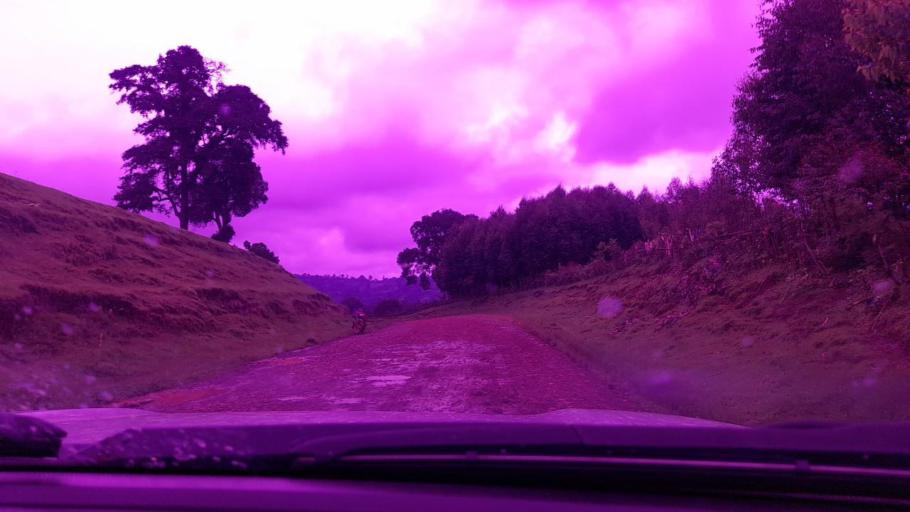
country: ET
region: Southern Nations, Nationalities, and People's Region
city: Tippi
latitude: 7.5645
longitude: 35.7903
